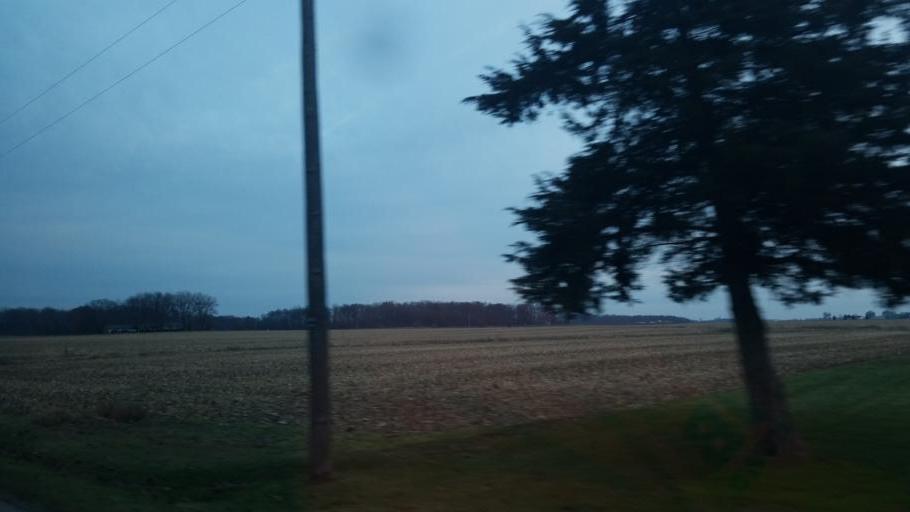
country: US
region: Indiana
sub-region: Adams County
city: Decatur
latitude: 40.7883
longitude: -84.9596
